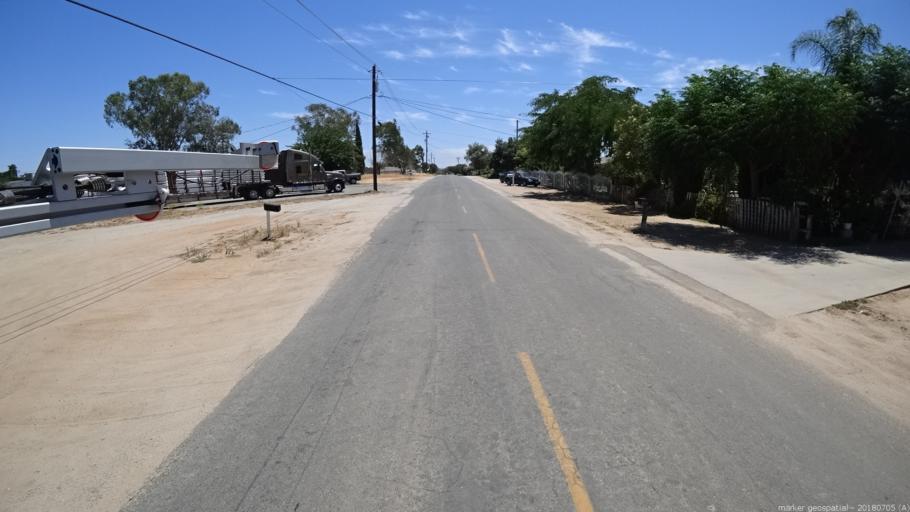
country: US
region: California
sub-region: Madera County
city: Madera
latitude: 36.9905
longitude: -120.0343
